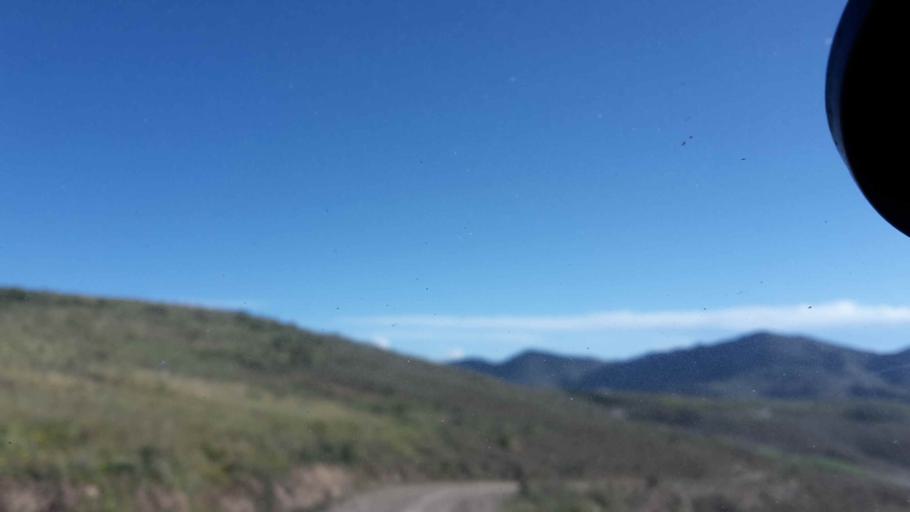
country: BO
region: Cochabamba
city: Arani
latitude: -17.7464
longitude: -65.6217
